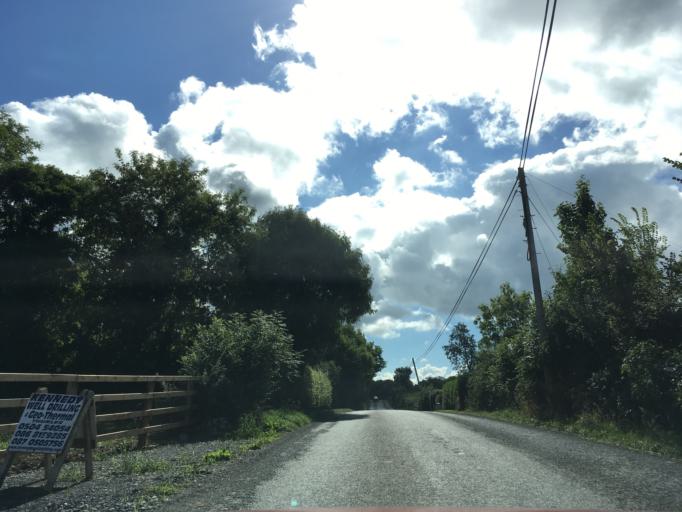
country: IE
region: Munster
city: Cashel
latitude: 52.4438
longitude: -7.8913
